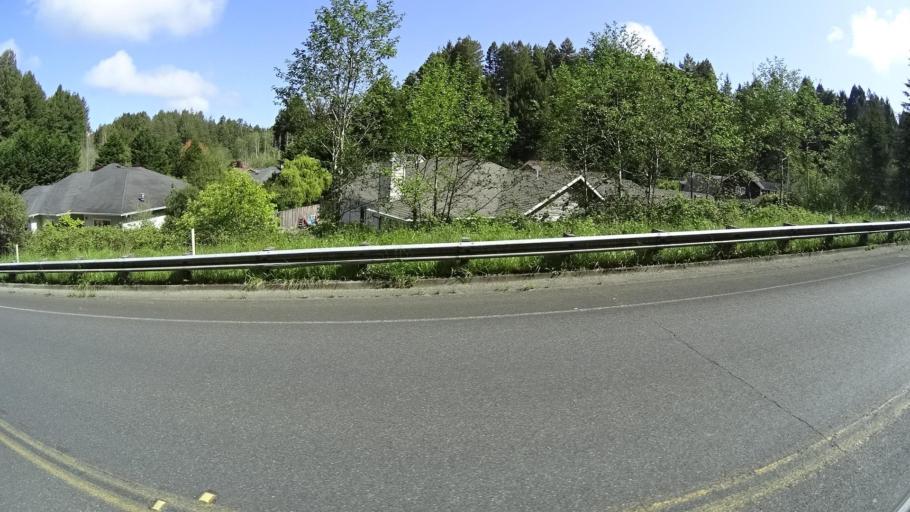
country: US
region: California
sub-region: Humboldt County
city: Cutten
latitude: 40.7675
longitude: -124.1566
